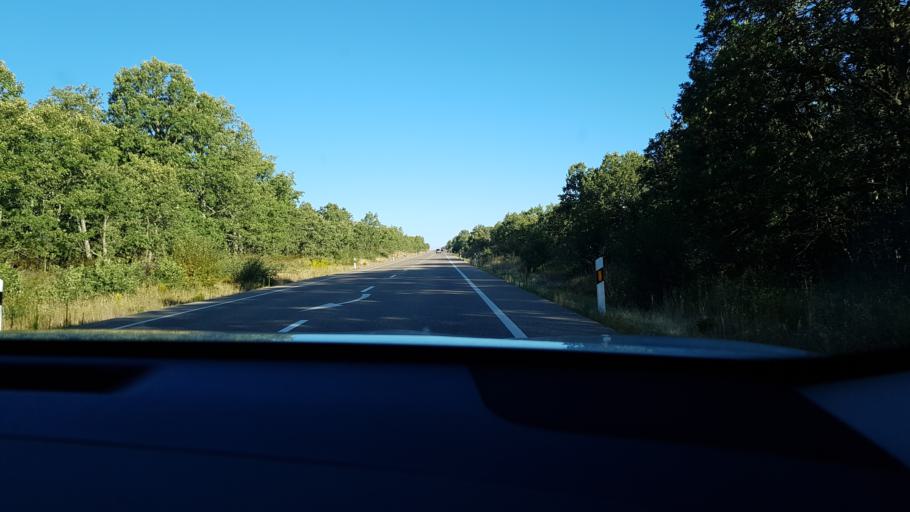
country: ES
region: Castille and Leon
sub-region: Provincia de Zamora
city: Samir de los Canos
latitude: 41.6722
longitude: -6.2341
